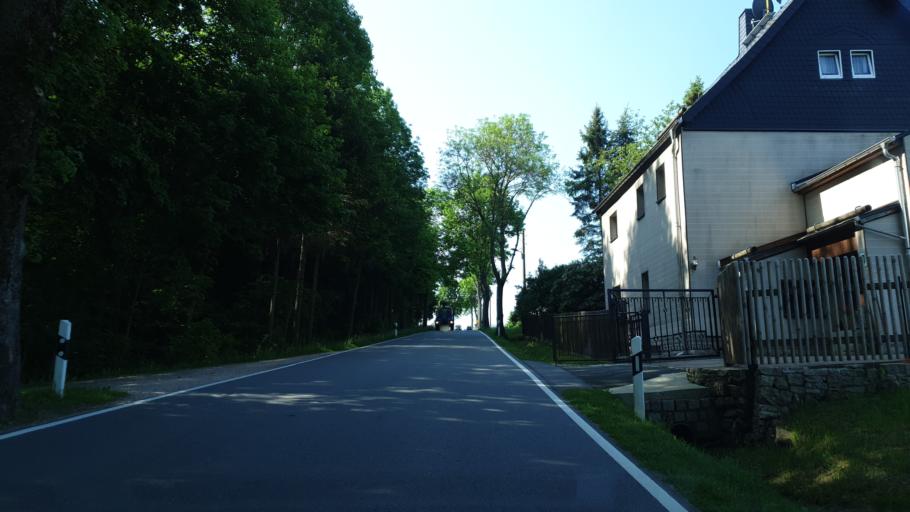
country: DE
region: Saxony
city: Zschorlau
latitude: 50.5432
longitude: 12.6227
